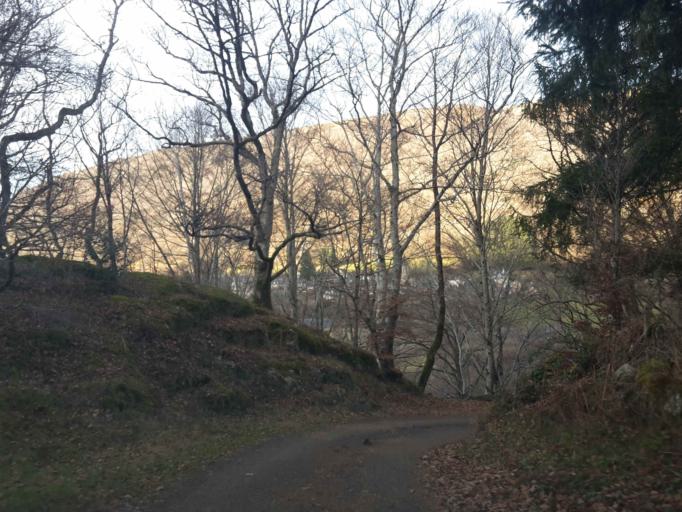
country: FR
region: Auvergne
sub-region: Departement du Cantal
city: Riom-es-Montagnes
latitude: 45.1845
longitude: 2.5680
